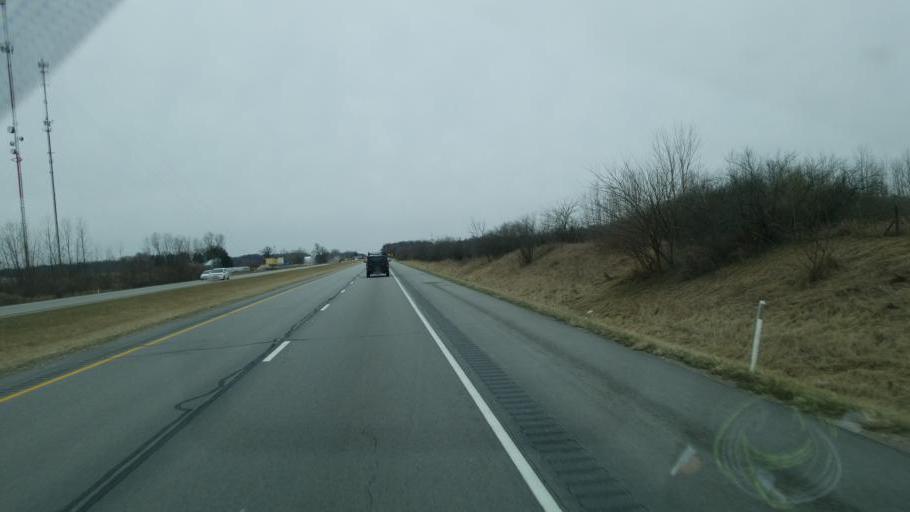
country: US
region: Indiana
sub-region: Marshall County
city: Plymouth
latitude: 41.3236
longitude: -86.2759
